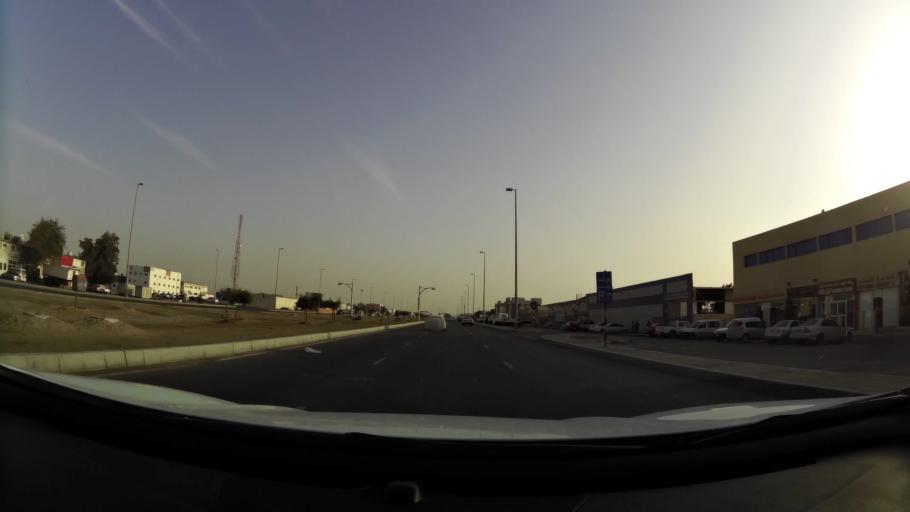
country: AE
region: Abu Dhabi
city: Abu Dhabi
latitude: 24.3650
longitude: 54.5112
